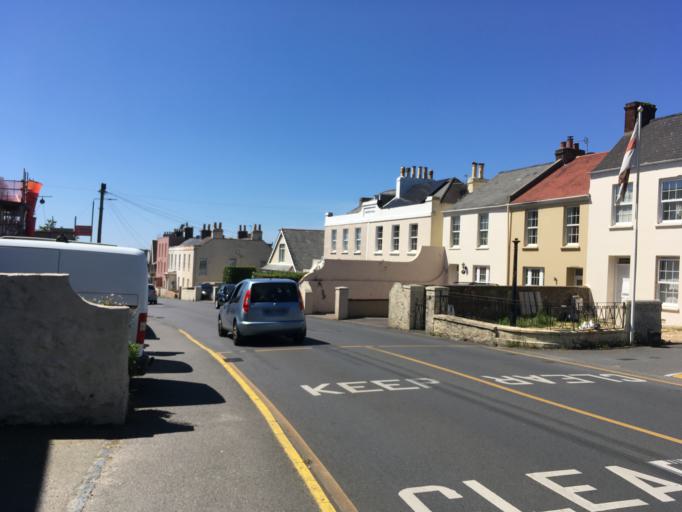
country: GG
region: St Peter Port
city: Saint Peter Port
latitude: 49.4596
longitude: -2.5559
